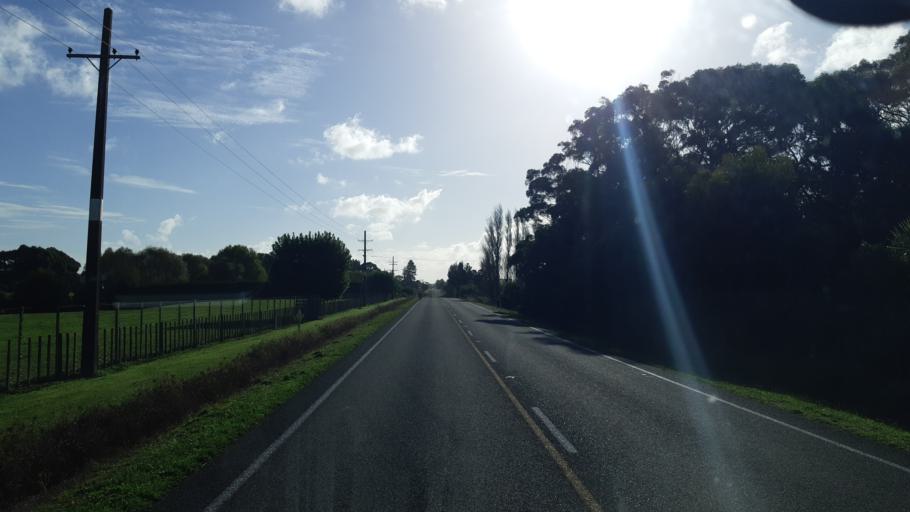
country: NZ
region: Manawatu-Wanganui
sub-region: Wanganui District
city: Wanganui
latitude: -39.9495
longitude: 175.1531
